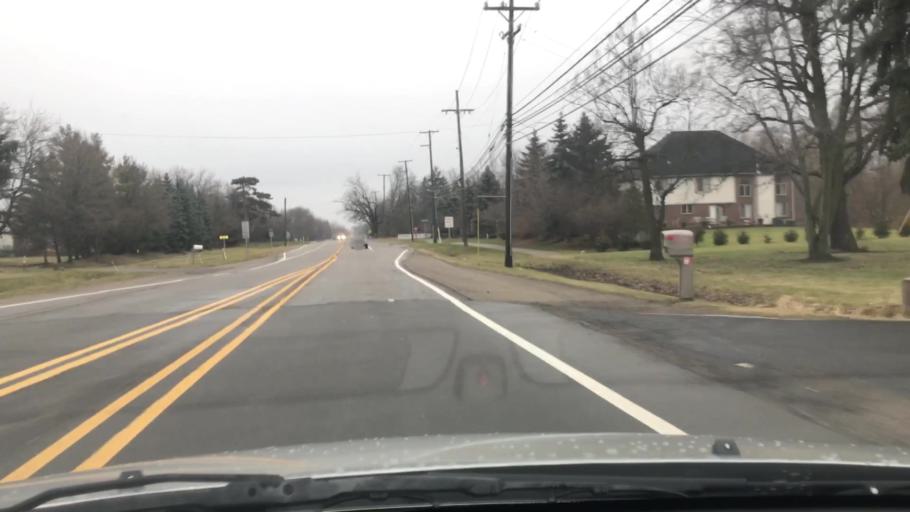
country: US
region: Michigan
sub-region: Oakland County
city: Troy
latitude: 42.6211
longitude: -83.1505
